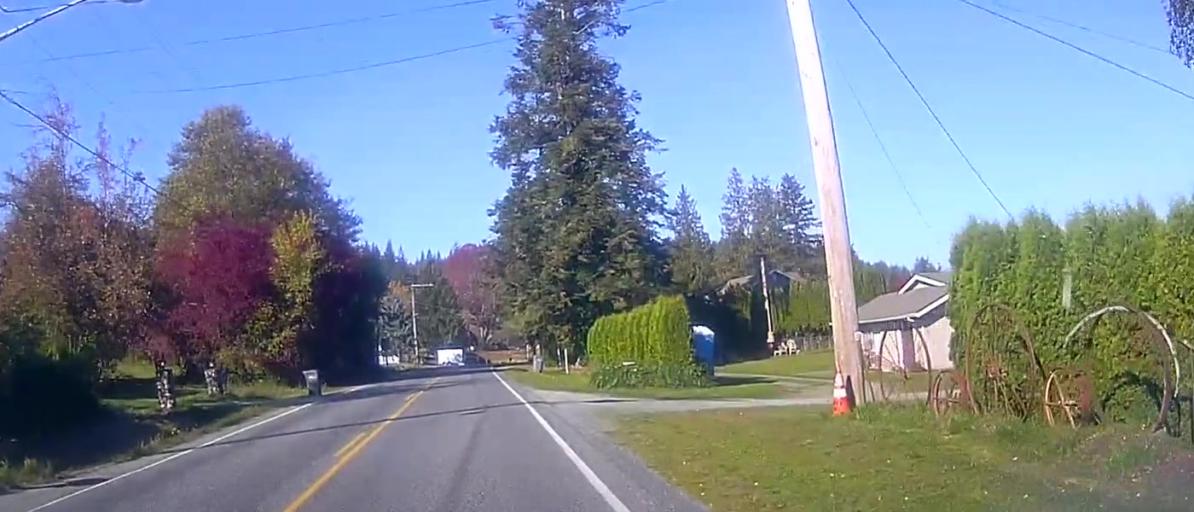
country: US
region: Washington
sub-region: Skagit County
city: Big Lake
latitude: 48.3908
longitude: -122.2457
